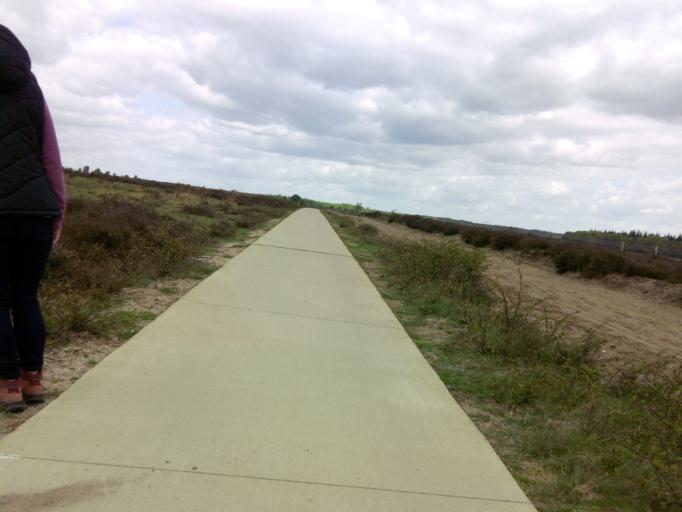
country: NL
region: Gelderland
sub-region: Gemeente Ede
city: Ede
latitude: 52.0427
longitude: 5.7181
